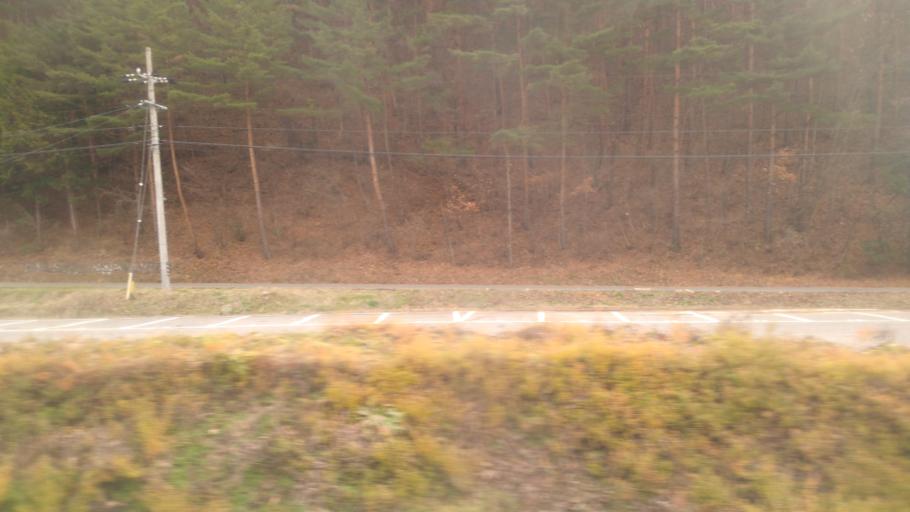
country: JP
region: Nagano
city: Ueda
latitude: 36.4568
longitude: 138.0793
